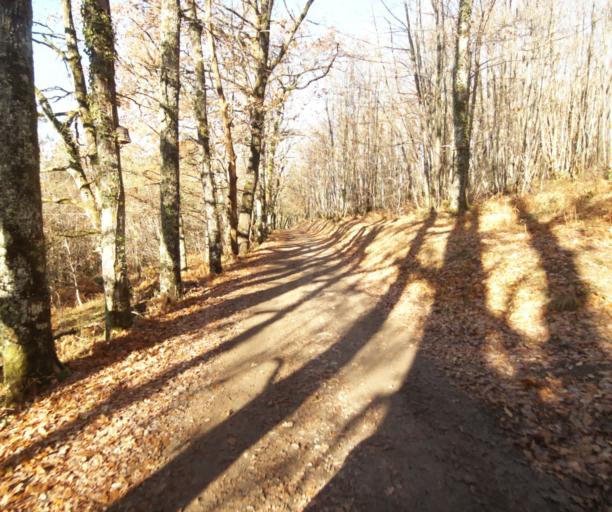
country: FR
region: Limousin
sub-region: Departement de la Correze
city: Sainte-Fortunade
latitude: 45.2171
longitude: 1.7776
